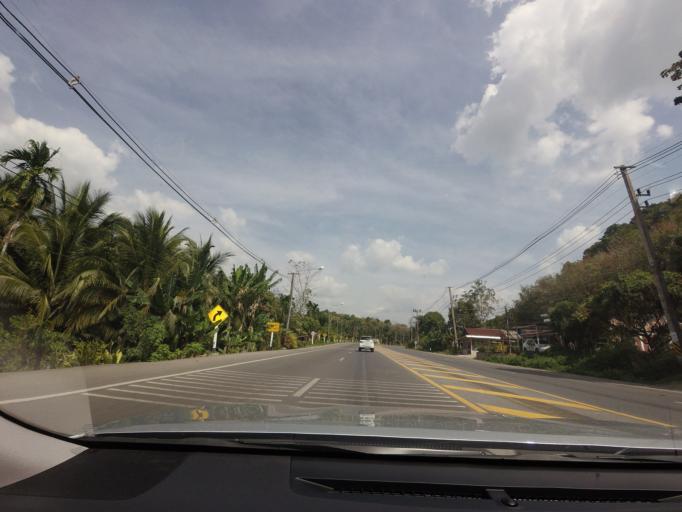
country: TH
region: Phangnga
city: Ban Ao Nang
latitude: 8.0522
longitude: 98.7696
